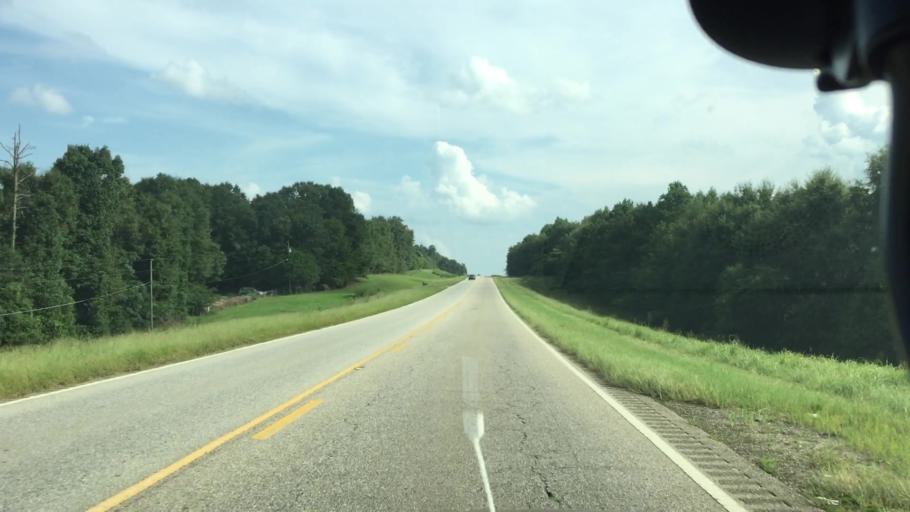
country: US
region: Alabama
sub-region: Pike County
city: Troy
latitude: 31.7179
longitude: -85.9599
